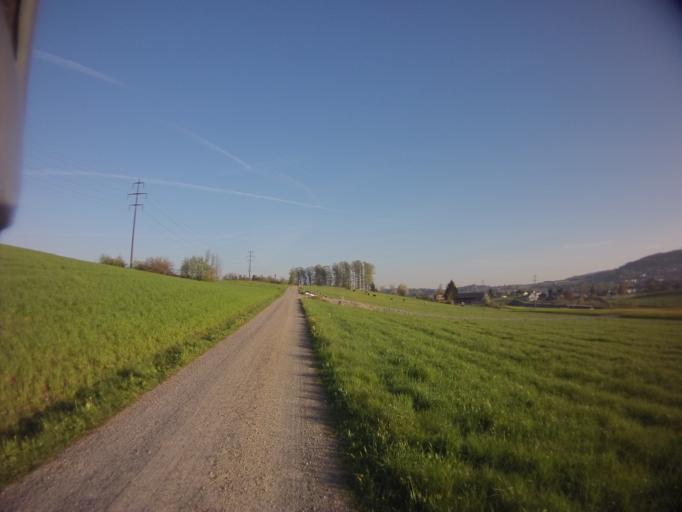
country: CH
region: Zurich
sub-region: Bezirk Affoltern
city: Mettmenstetten
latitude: 47.2355
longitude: 8.4553
